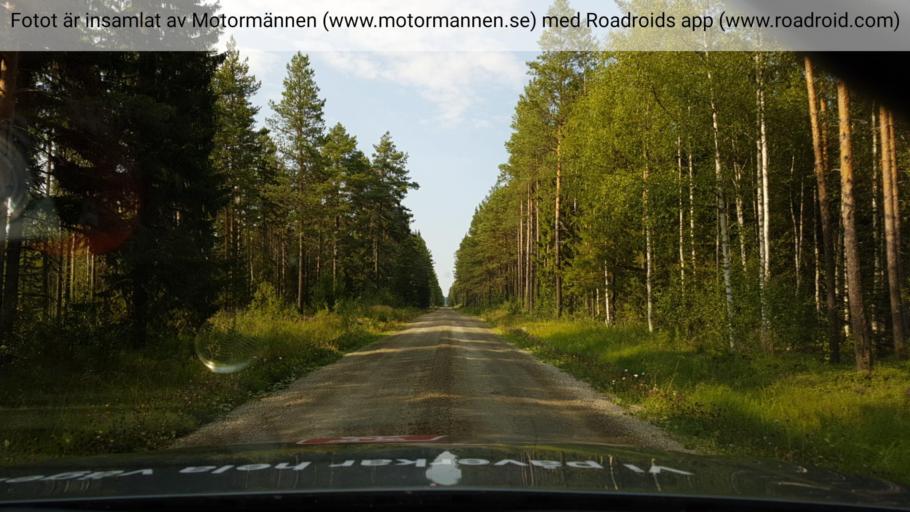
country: SE
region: Jaemtland
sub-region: Braecke Kommun
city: Braecke
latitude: 62.4878
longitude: 14.9246
